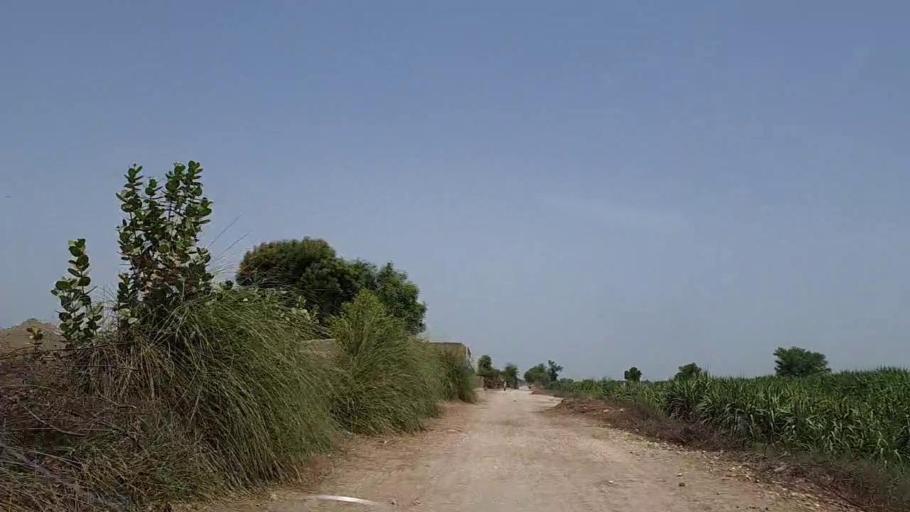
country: PK
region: Sindh
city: Tharu Shah
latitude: 26.9120
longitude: 68.0032
